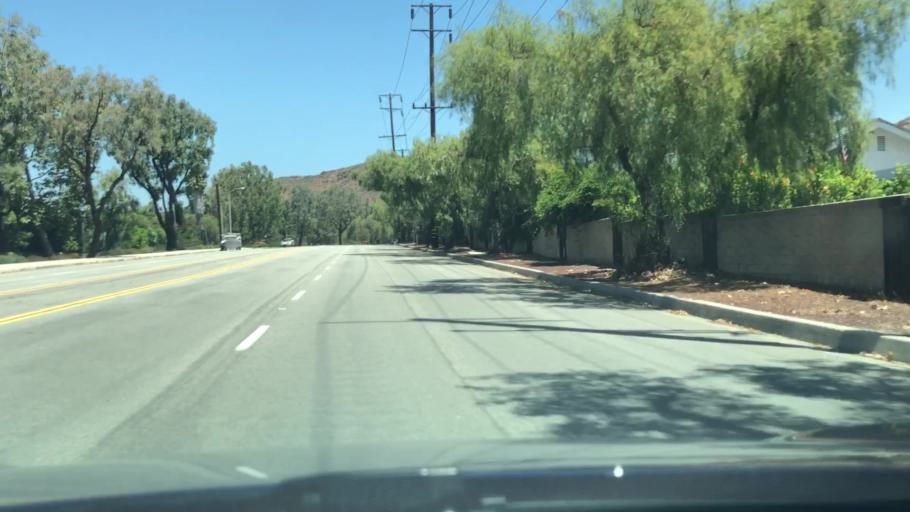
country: US
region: California
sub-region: Ventura County
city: Casa Conejo
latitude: 34.1879
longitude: -118.9542
